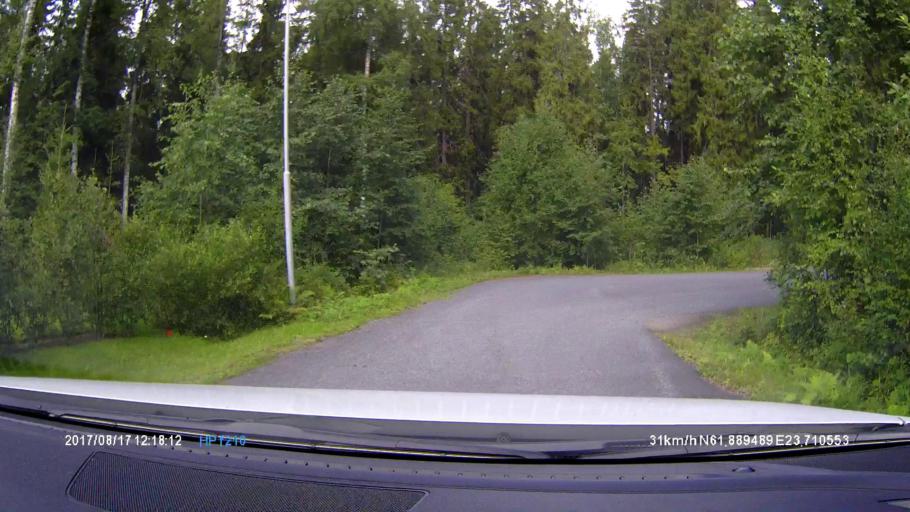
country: FI
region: Pirkanmaa
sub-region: Tampere
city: Kuru
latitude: 61.8898
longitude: 23.7102
